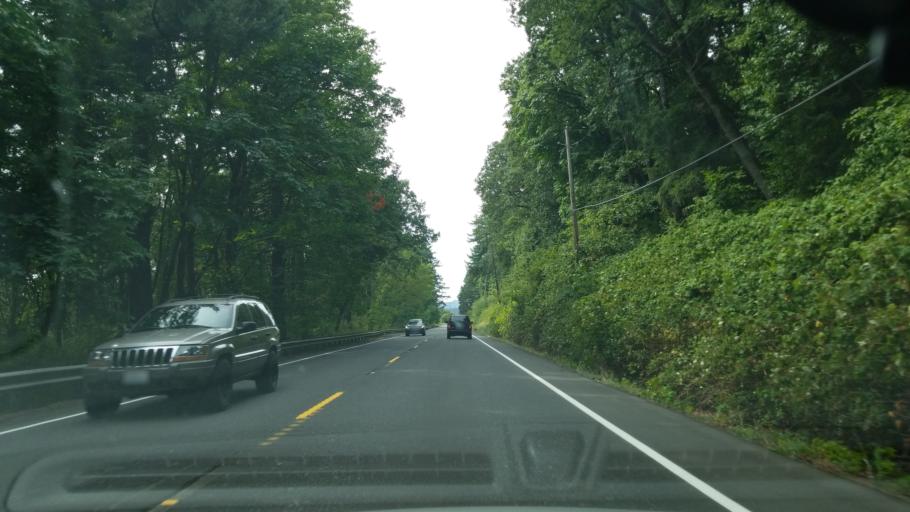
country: US
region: Washington
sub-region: Clark County
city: Washougal
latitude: 45.5674
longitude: -122.2862
